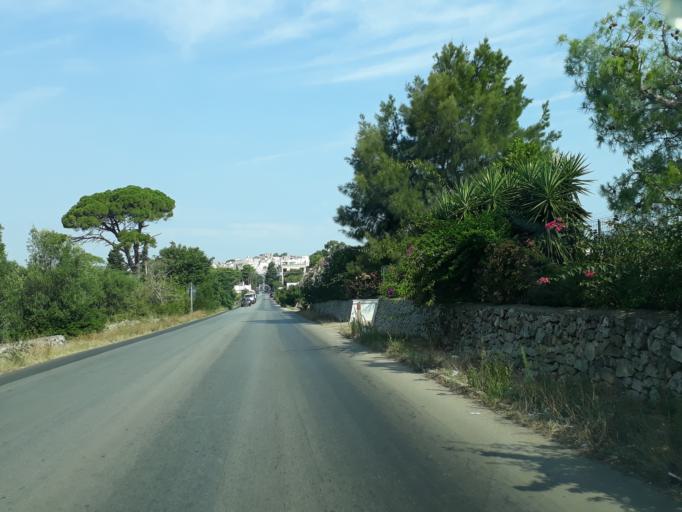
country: IT
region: Apulia
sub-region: Provincia di Brindisi
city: Carovigno
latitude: 40.6963
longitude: 17.6680
